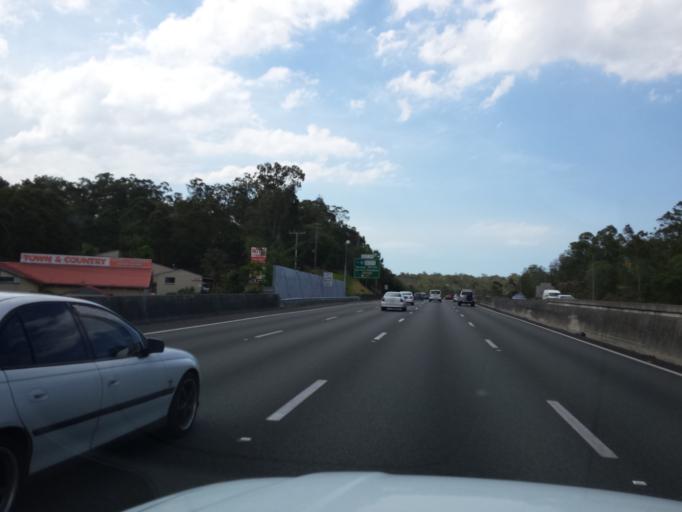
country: AU
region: Queensland
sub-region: Gold Coast
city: Nerang
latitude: -27.9848
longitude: 153.3414
